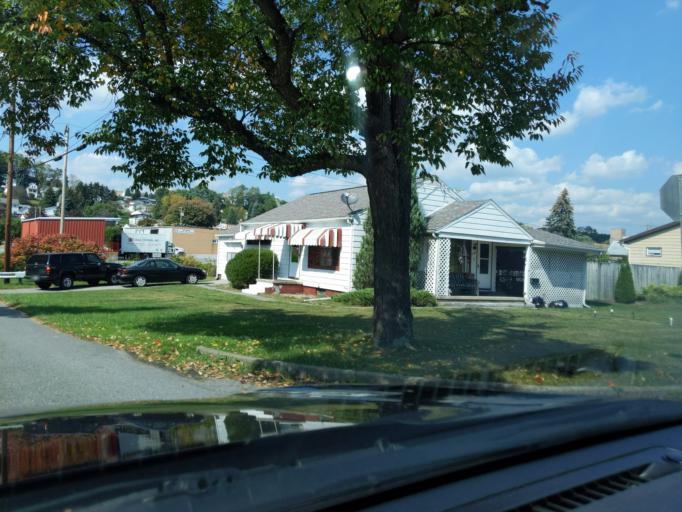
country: US
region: Pennsylvania
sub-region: Blair County
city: Altoona
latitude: 40.5047
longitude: -78.3869
